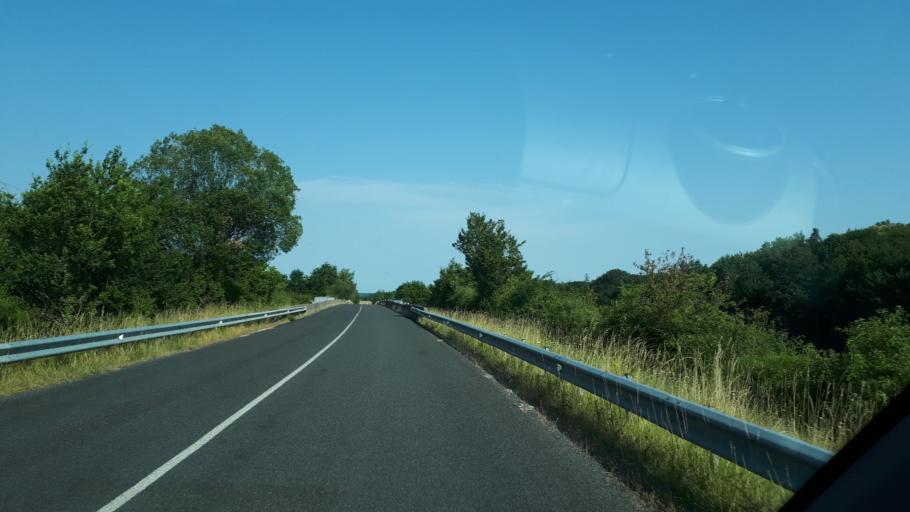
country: FR
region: Centre
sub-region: Departement du Loir-et-Cher
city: La Ville-aux-Clercs
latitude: 47.9692
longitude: 1.0503
